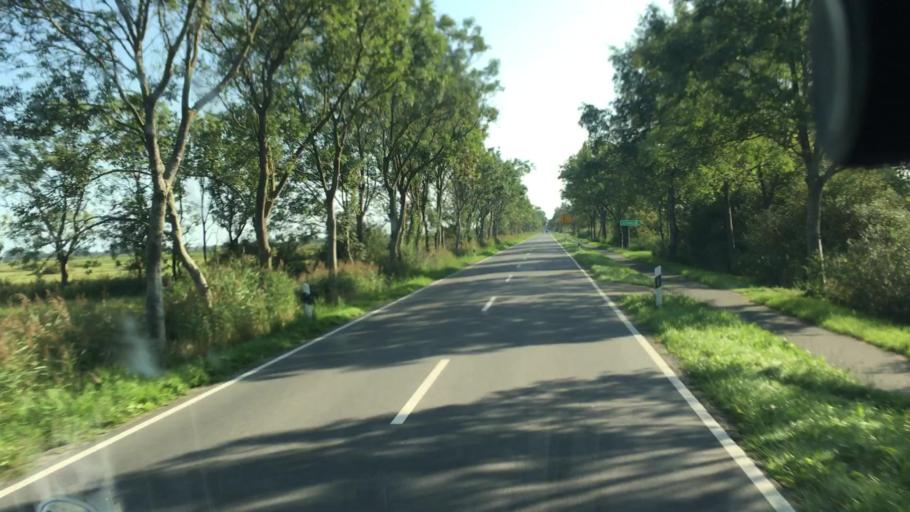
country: DE
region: Lower Saxony
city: Esens
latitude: 53.6570
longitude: 7.6427
